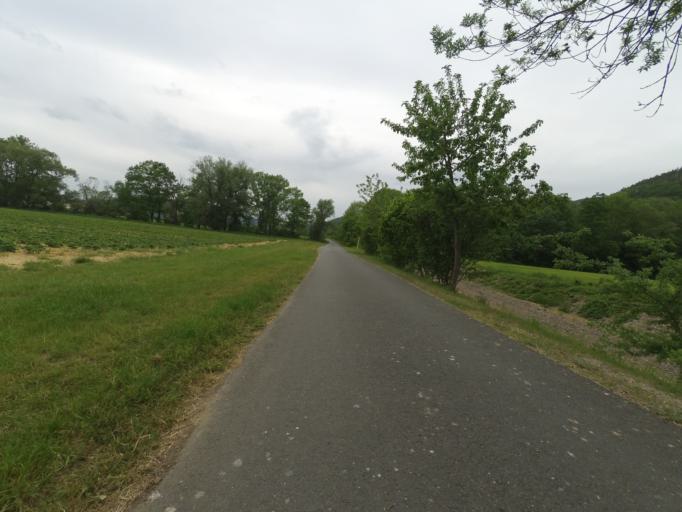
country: DE
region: Thuringia
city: Bad Blankenburg
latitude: 50.6865
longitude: 11.2967
